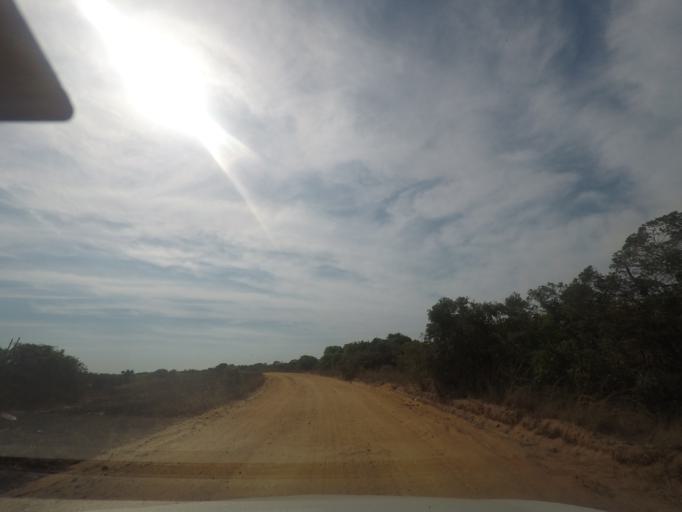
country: BR
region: Rio de Janeiro
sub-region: Marica
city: Marica
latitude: -22.9574
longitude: -42.8834
